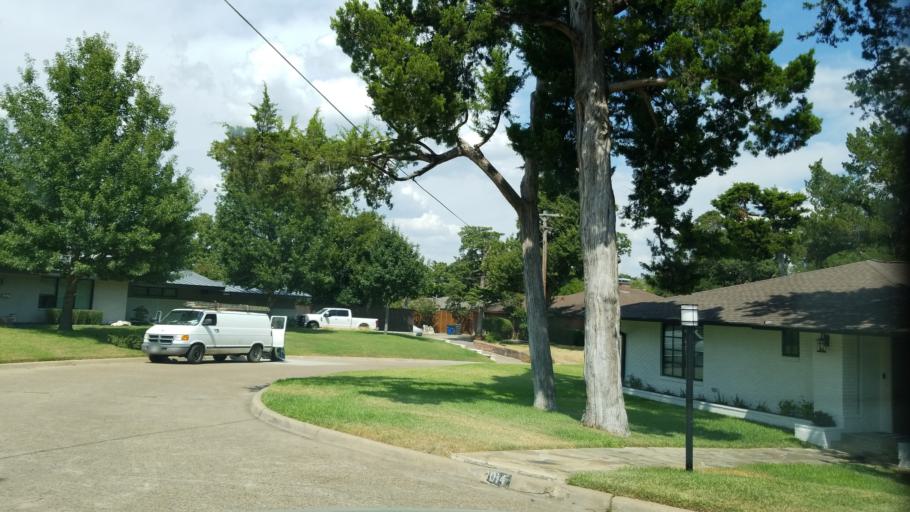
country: US
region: Texas
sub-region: Dallas County
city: Dallas
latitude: 32.7635
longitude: -96.8395
